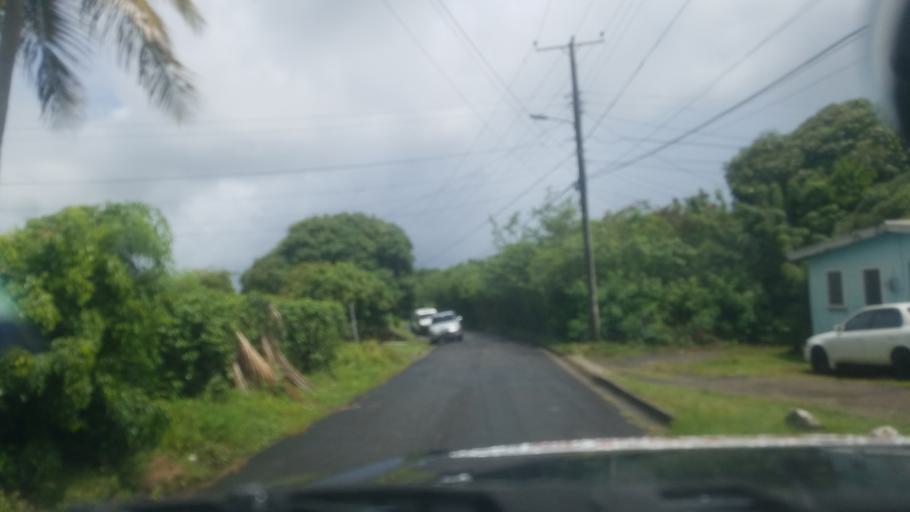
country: LC
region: Laborie Quarter
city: Laborie
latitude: 13.7566
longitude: -60.9757
